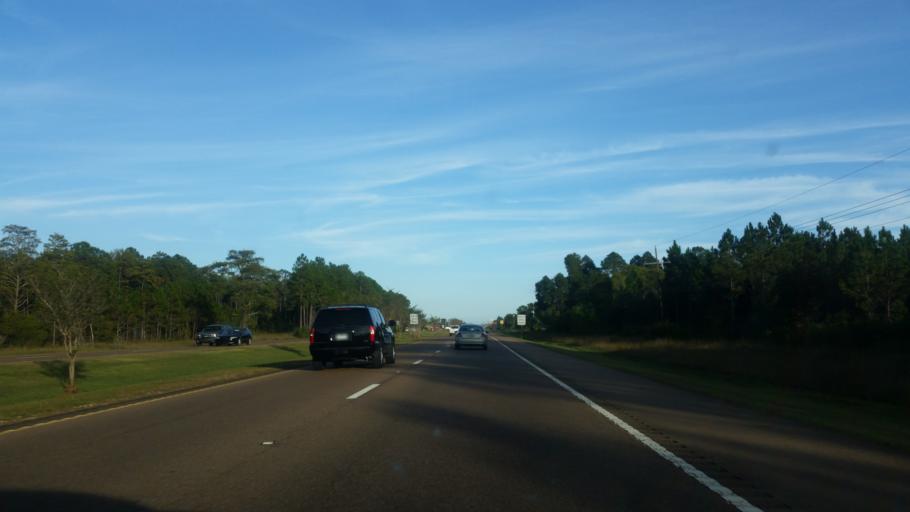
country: US
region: Mississippi
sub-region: Jackson County
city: Gautier
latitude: 30.3954
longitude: -88.6754
